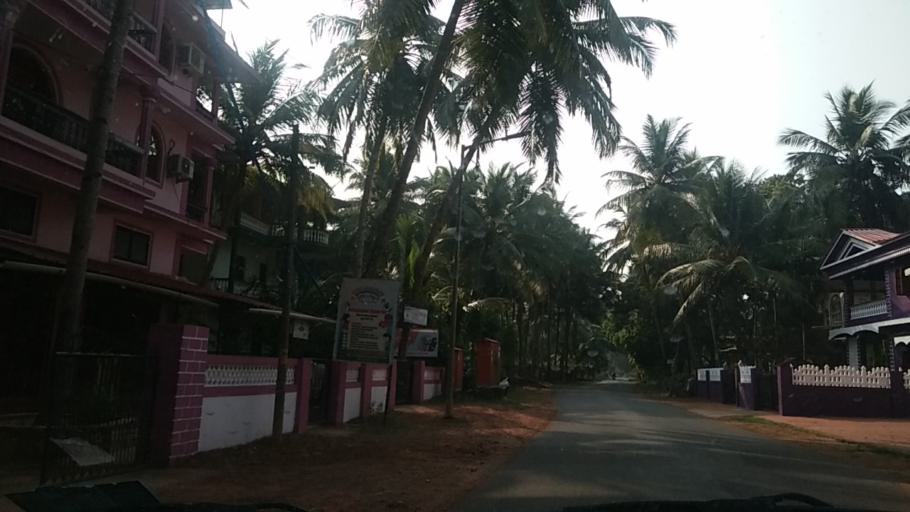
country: IN
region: Goa
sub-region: South Goa
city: Colva
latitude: 15.3077
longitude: 73.9359
